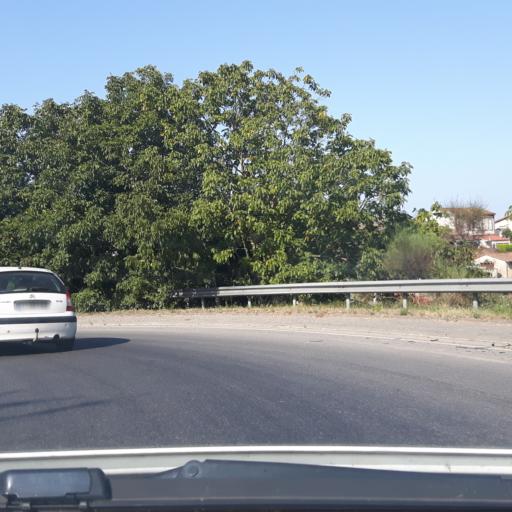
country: FR
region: Midi-Pyrenees
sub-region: Departement de la Haute-Garonne
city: Ondes
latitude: 43.7798
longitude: 1.3079
